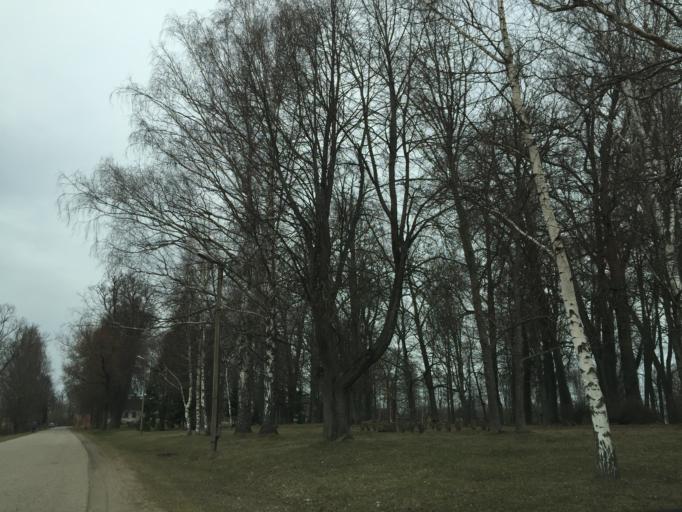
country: LV
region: Ilukste
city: Ilukste
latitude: 56.0551
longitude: 26.2831
